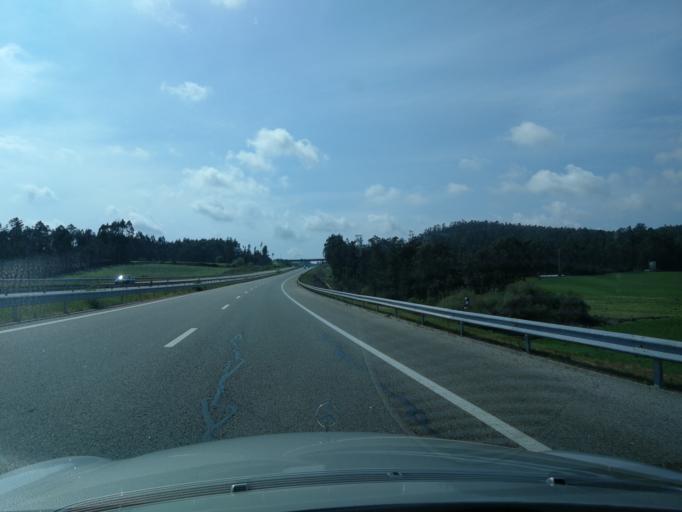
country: PT
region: Braga
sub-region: Vila Nova de Famalicao
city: Ribeirao
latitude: 41.3831
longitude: -8.6322
